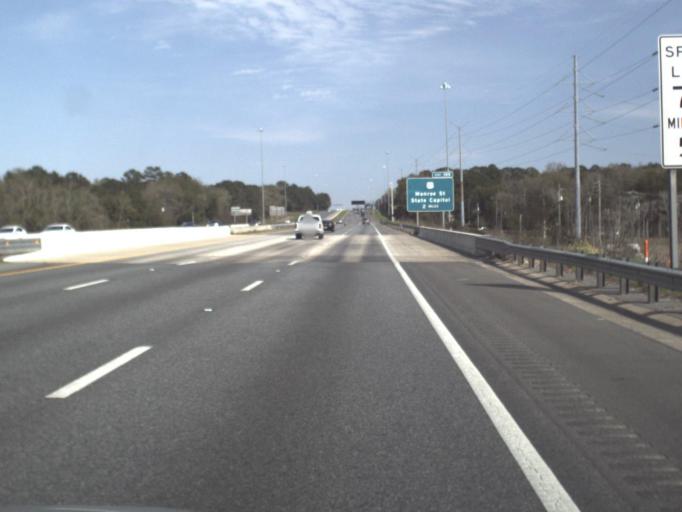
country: US
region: Florida
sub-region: Leon County
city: Tallahassee
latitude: 30.4781
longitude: -84.3474
